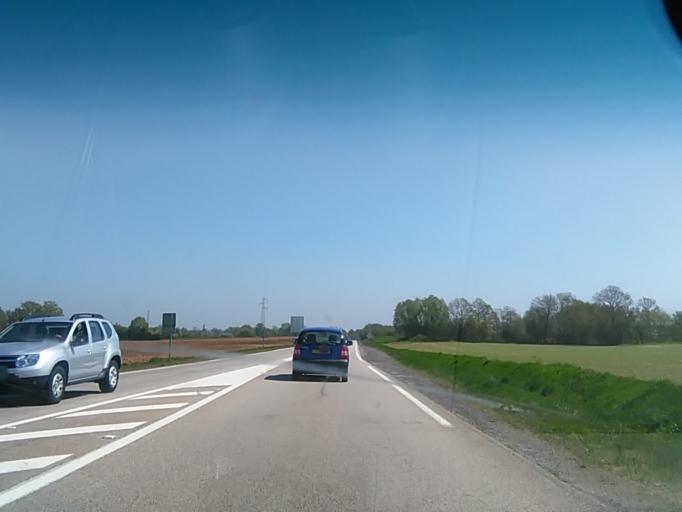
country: FR
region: Lower Normandy
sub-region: Departement de l'Orne
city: Aube-sur-Rile
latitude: 48.7302
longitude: 0.5552
